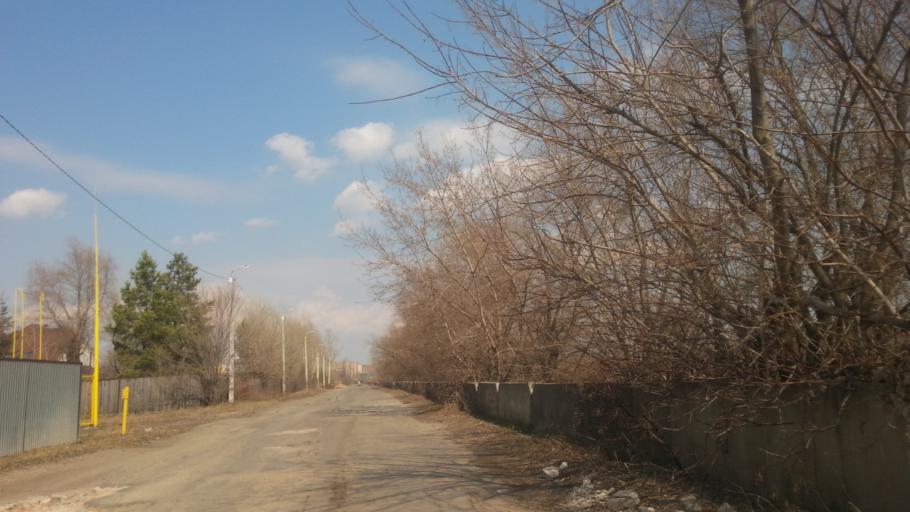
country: RU
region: Altai Krai
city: Yuzhnyy
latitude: 53.3089
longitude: 83.7207
